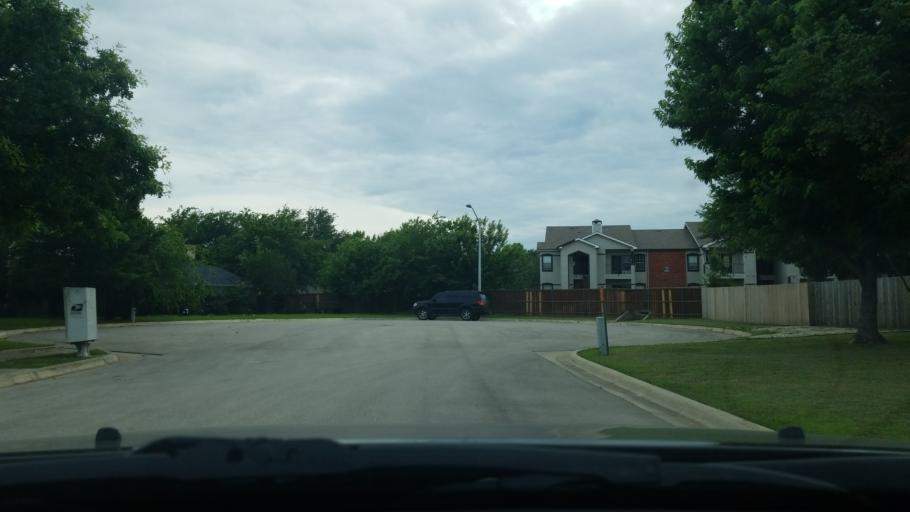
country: US
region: Texas
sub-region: Denton County
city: Denton
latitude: 33.2454
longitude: -97.1288
